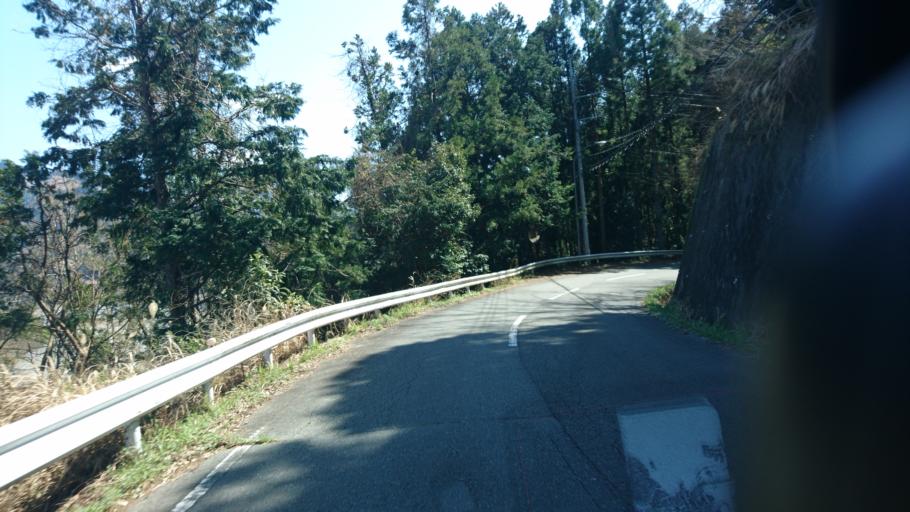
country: JP
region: Shizuoka
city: Fujinomiya
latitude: 35.3493
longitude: 138.4378
